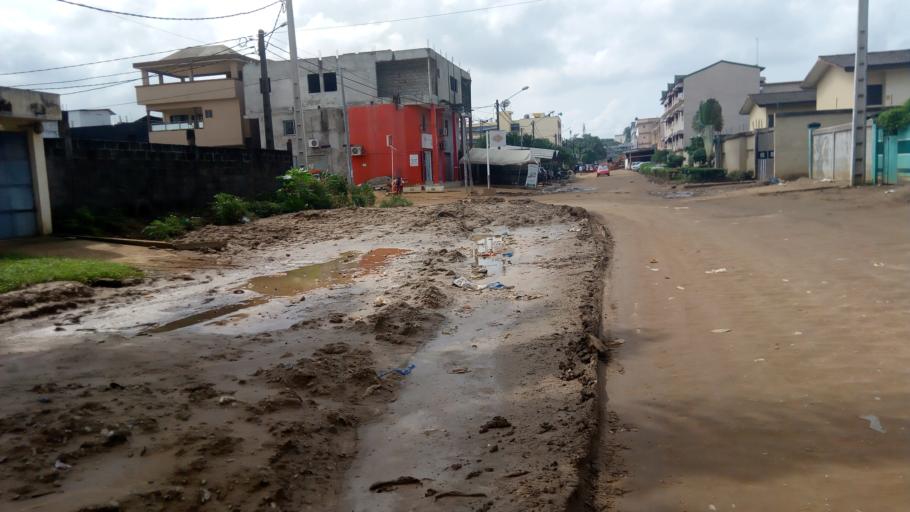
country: CI
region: Lagunes
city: Bingerville
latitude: 5.3658
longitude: -3.9595
